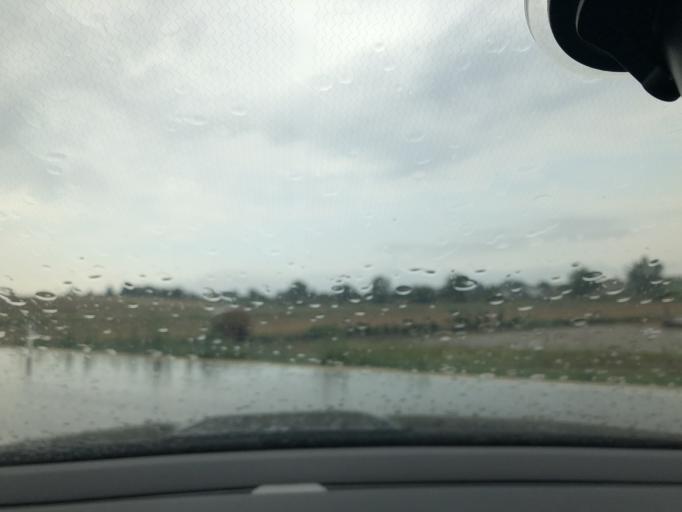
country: AT
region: Lower Austria
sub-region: Politischer Bezirk Ganserndorf
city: Auersthal
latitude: 48.3671
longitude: 16.6519
